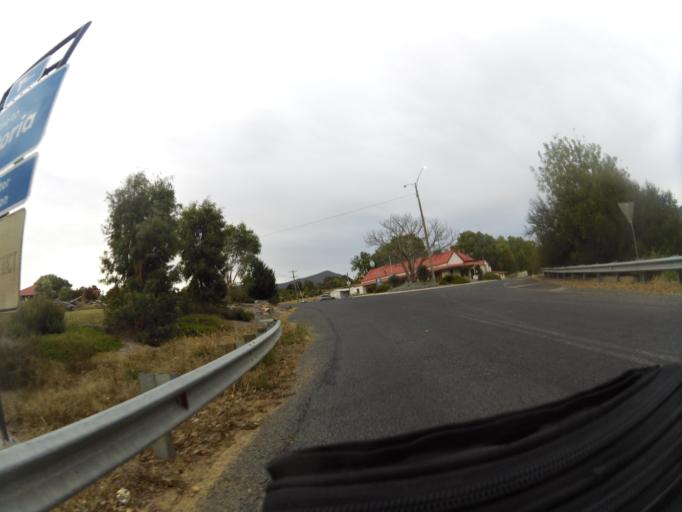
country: AU
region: New South Wales
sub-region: Greater Hume Shire
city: Holbrook
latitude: -36.0463
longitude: 147.9315
